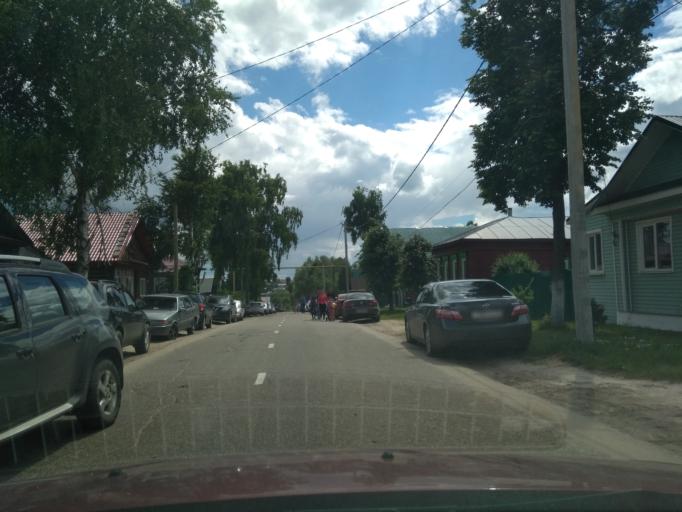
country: RU
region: Vladimir
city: Melenki
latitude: 55.3404
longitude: 41.6361
